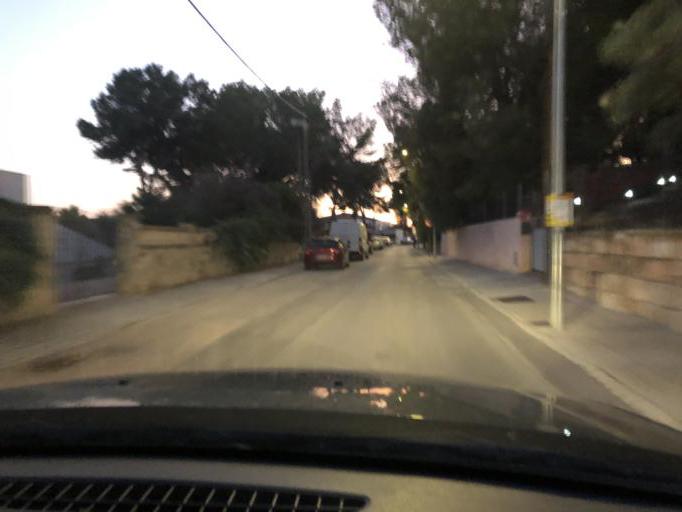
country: ES
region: Balearic Islands
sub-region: Illes Balears
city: Santa Ponsa
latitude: 39.5226
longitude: 2.4893
